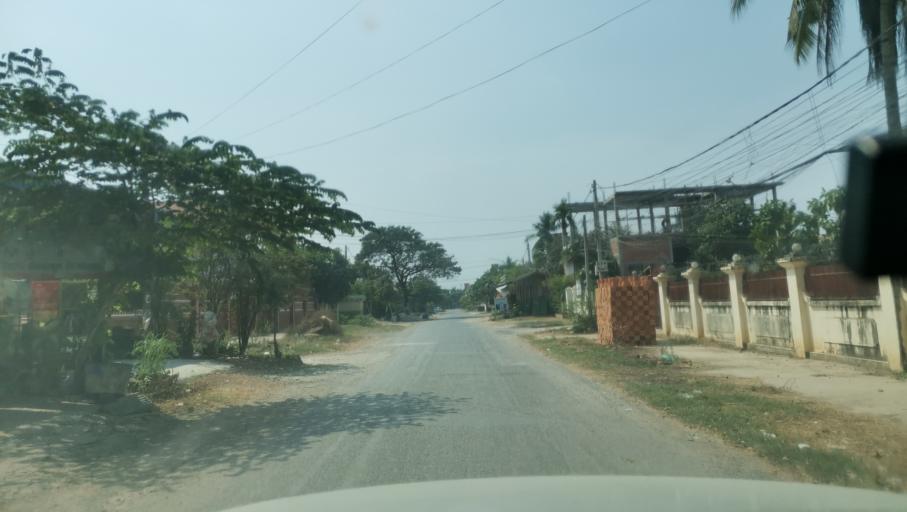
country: KH
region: Battambang
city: Battambang
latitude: 13.0881
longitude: 103.1959
